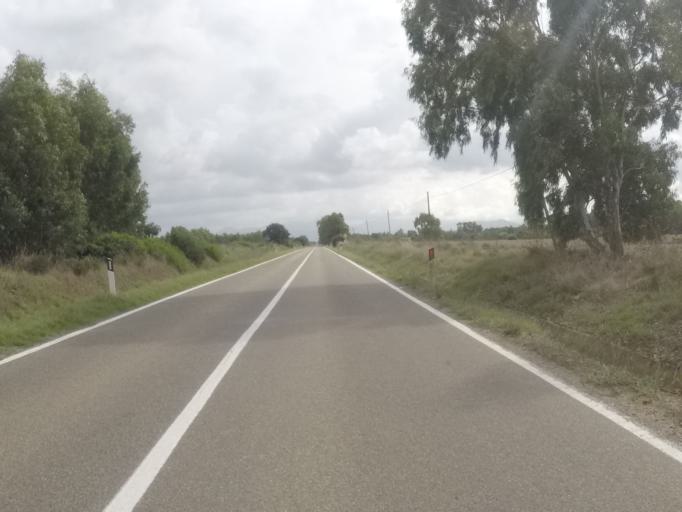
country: IT
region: Sardinia
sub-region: Provincia di Oristano
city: San Nicolo d'Arcidano
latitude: 39.6551
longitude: 8.6536
